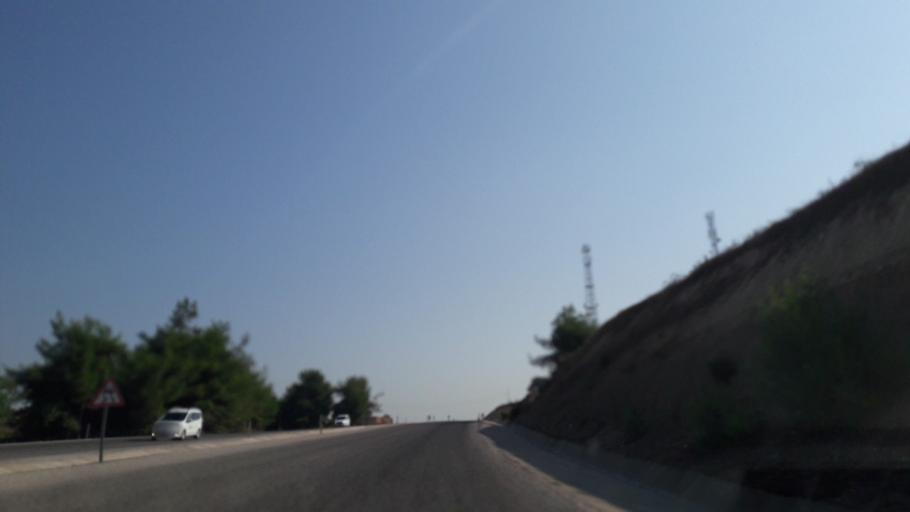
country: TR
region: Adana
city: Sagkaya
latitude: 37.1798
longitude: 35.5690
